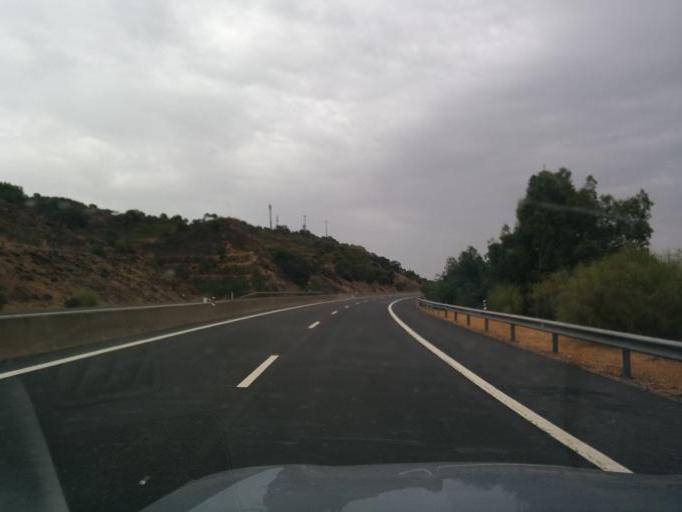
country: PT
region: Faro
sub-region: Tavira
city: Tavira
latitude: 37.1586
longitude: -7.6646
